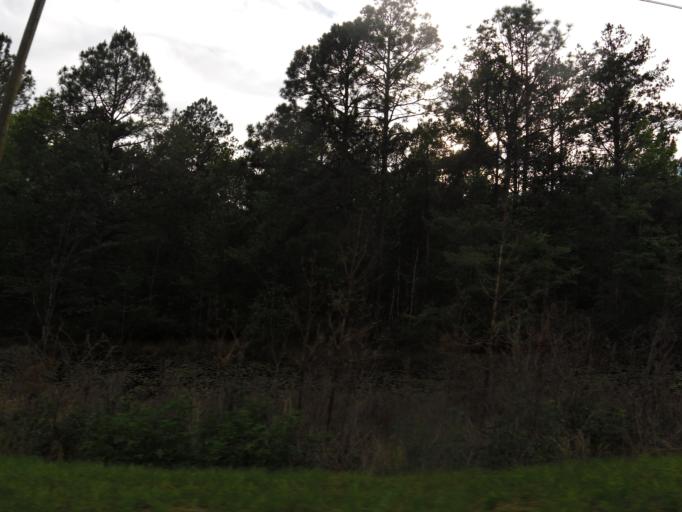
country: US
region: South Carolina
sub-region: Jasper County
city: Hardeeville
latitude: 32.3344
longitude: -81.0910
